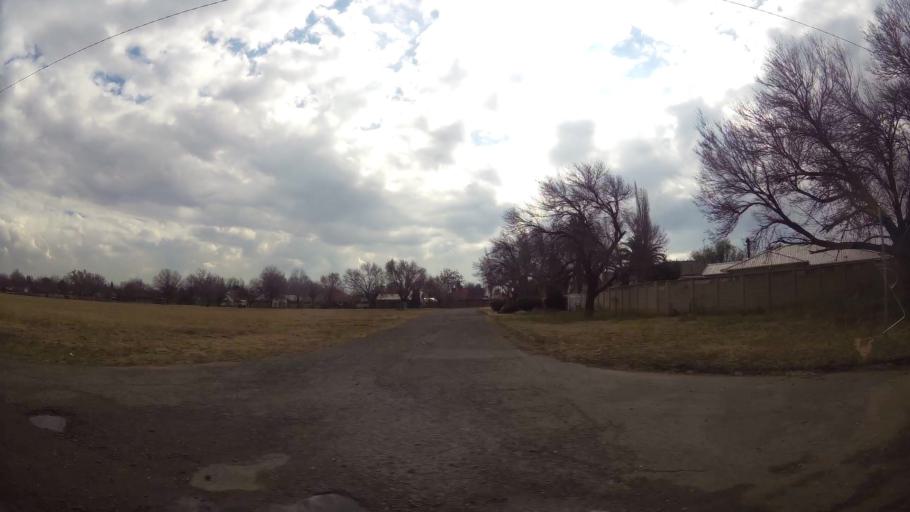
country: ZA
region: Gauteng
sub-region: Sedibeng District Municipality
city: Vereeniging
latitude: -26.6540
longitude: 27.9874
